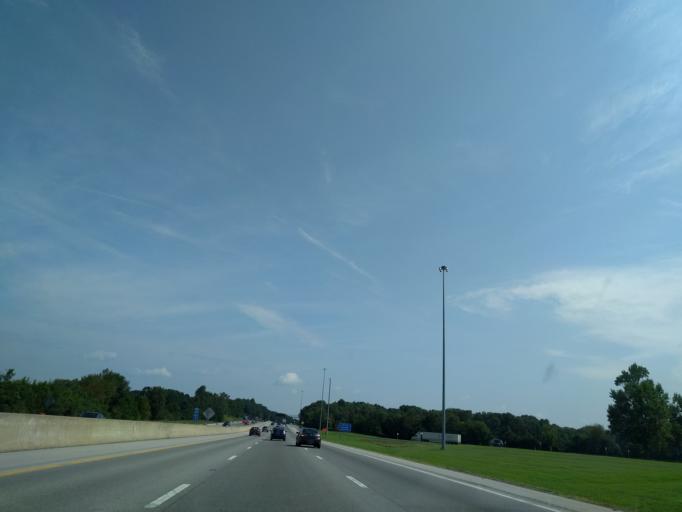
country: US
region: Kentucky
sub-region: Simpson County
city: Franklin
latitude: 36.6440
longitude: -86.5696
